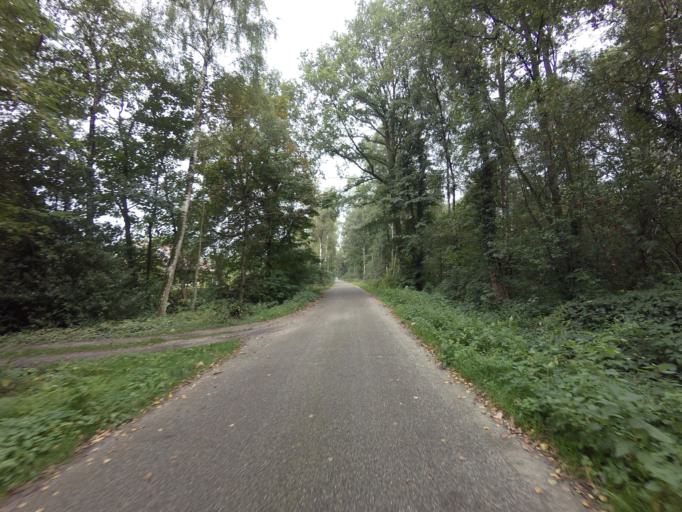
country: NL
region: Overijssel
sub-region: Gemeente Enschede
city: Enschede
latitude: 52.1812
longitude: 6.9389
